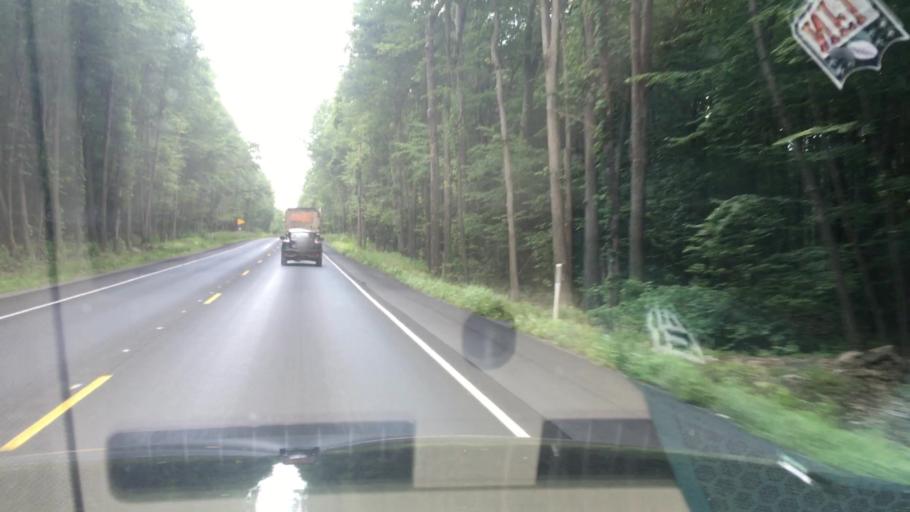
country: US
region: Pennsylvania
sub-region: Northumberland County
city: Mount Carmel
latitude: 40.7678
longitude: -76.4192
